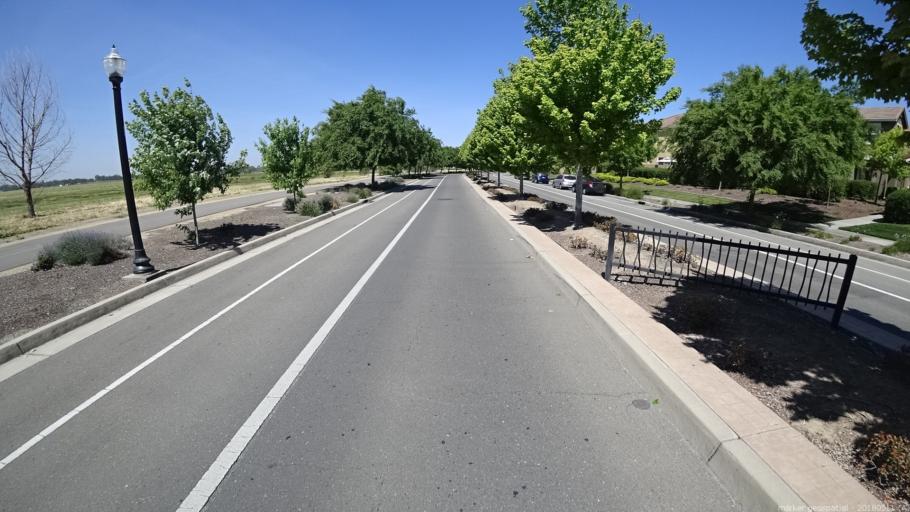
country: US
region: California
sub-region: Yolo County
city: West Sacramento
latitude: 38.6434
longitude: -121.5422
